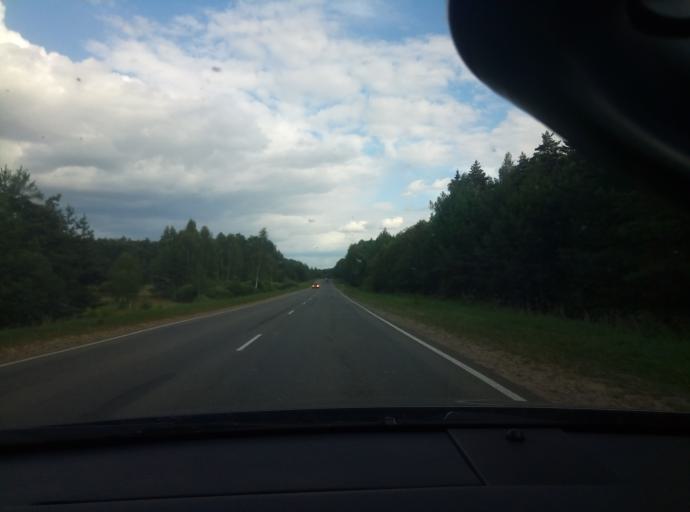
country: RU
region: Kaluga
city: Nikola-Lenivets
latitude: 54.5408
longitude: 35.5451
